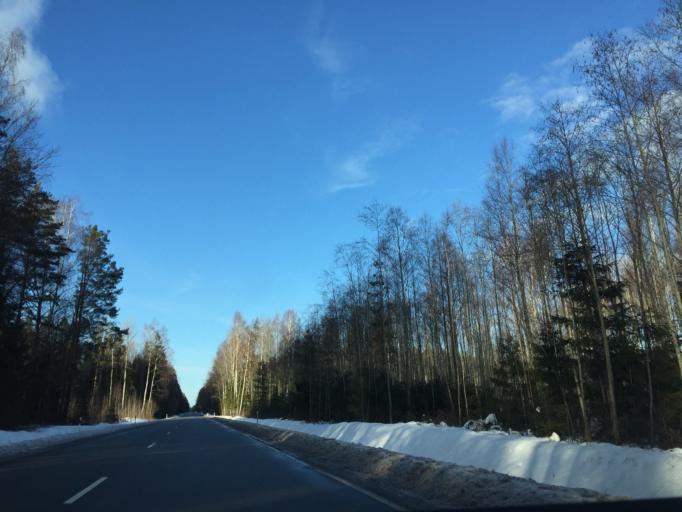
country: LV
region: Lielvarde
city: Lielvarde
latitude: 56.6636
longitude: 24.8684
